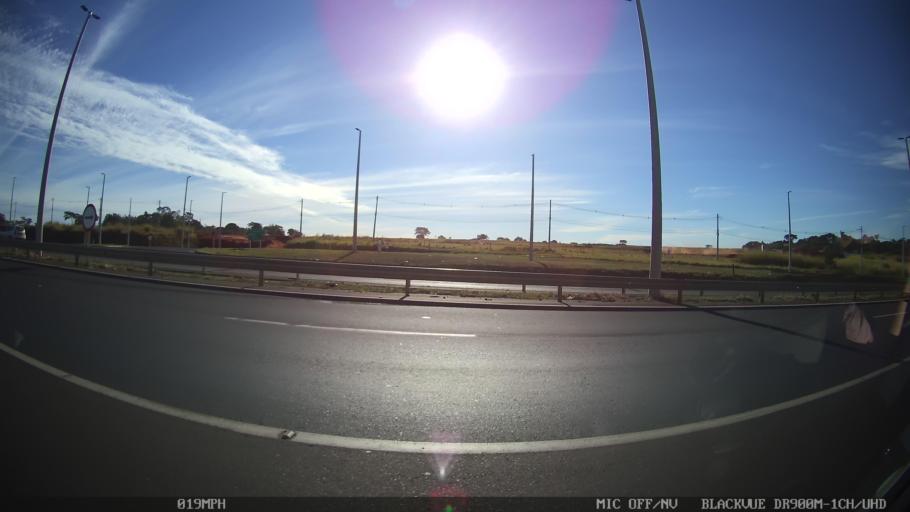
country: BR
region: Sao Paulo
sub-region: Bady Bassitt
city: Bady Bassitt
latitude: -20.8776
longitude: -49.4207
